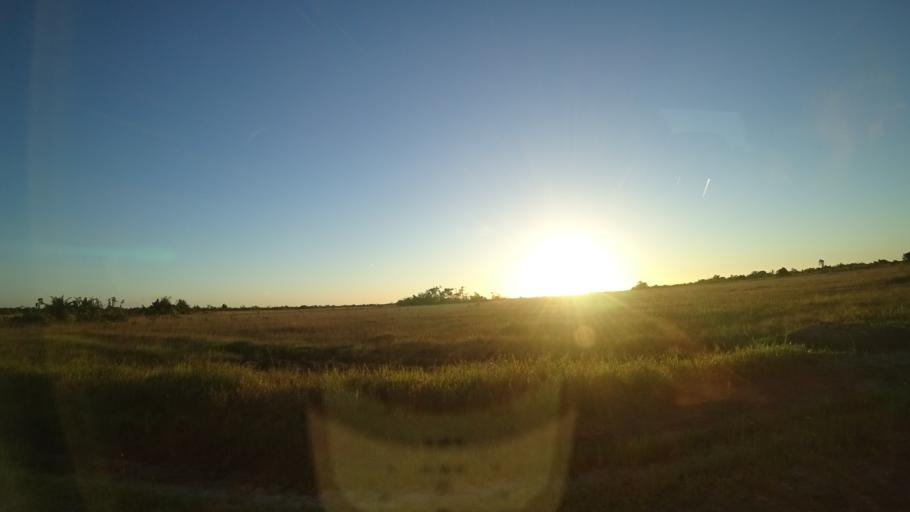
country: MZ
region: Sofala
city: Beira
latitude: -19.6604
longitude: 35.0625
